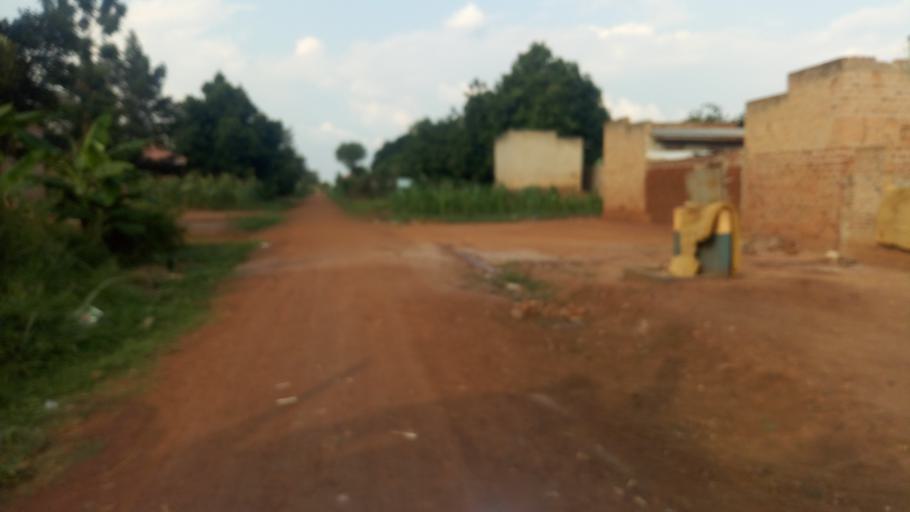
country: UG
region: Western Region
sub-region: Kiryandongo District
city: Kiryandongo
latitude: 1.8030
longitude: 32.0064
